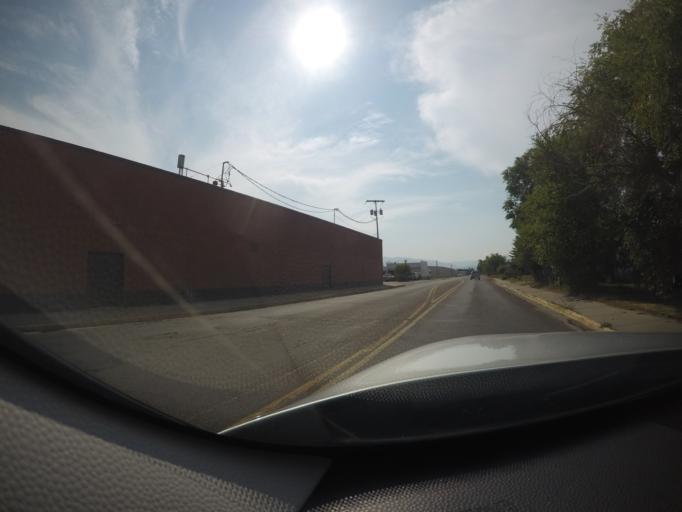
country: US
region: Montana
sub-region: Missoula County
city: Missoula
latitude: 46.8561
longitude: -114.0081
